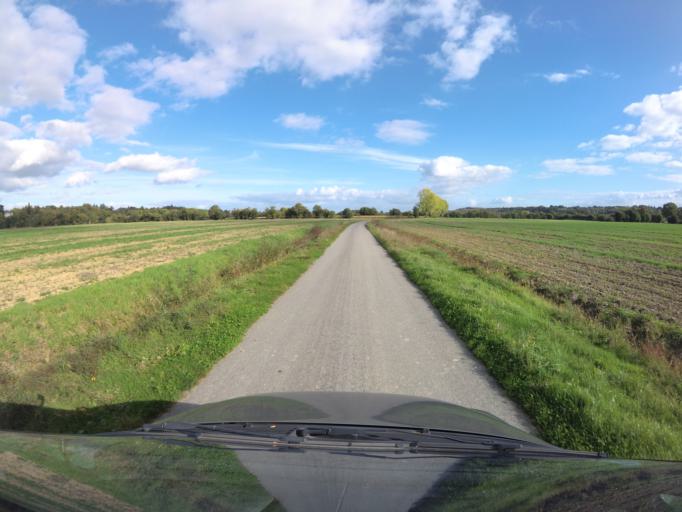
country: FR
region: Brittany
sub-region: Departement du Morbihan
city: Saint-Martin-sur-Oust
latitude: 47.7369
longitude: -2.2396
